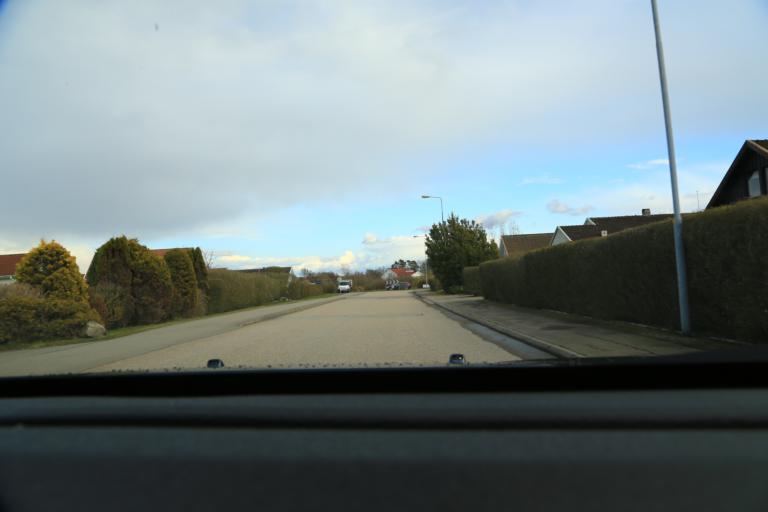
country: SE
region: Halland
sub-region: Varbergs Kommun
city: Traslovslage
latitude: 57.0505
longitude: 12.2886
